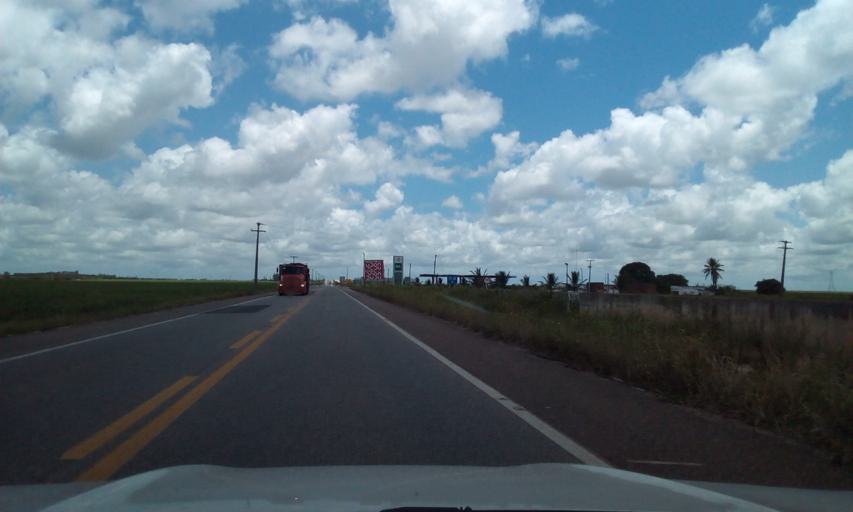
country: BR
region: Alagoas
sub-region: Campo Alegre
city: Campo Alegre
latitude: -9.9000
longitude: -36.2717
